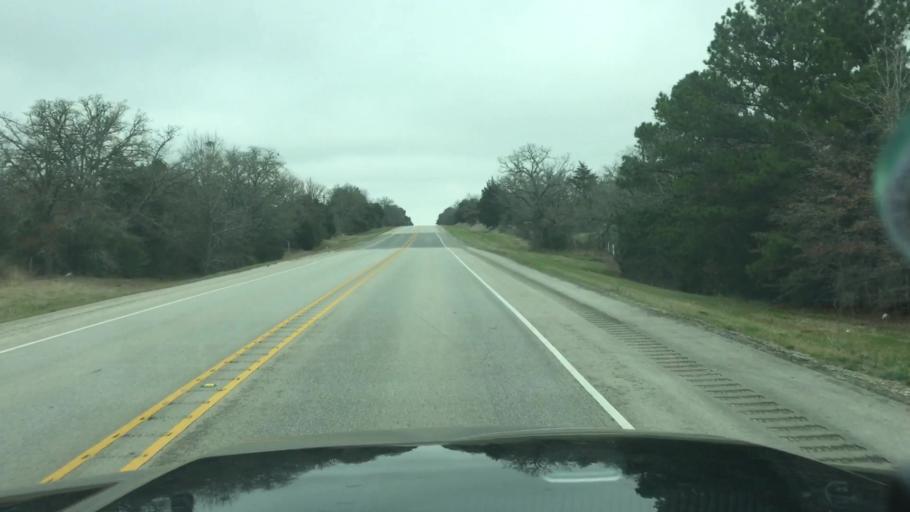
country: US
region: Texas
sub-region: Lee County
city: Giddings
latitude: 30.0737
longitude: -96.9169
